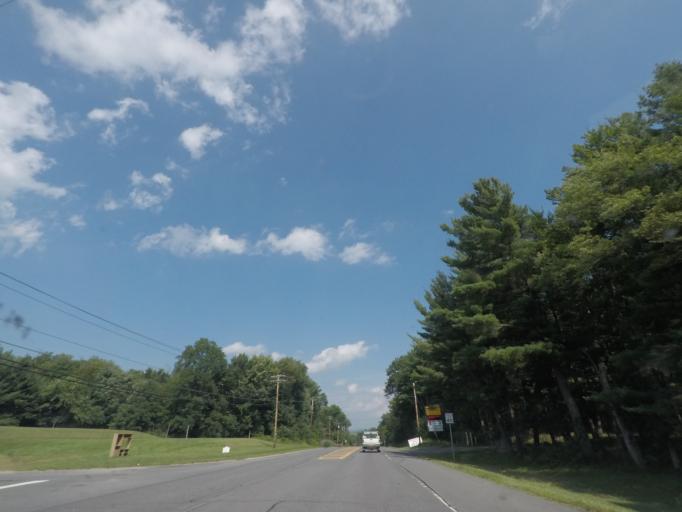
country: US
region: New York
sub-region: Rensselaer County
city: Poestenkill
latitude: 42.8074
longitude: -73.5453
